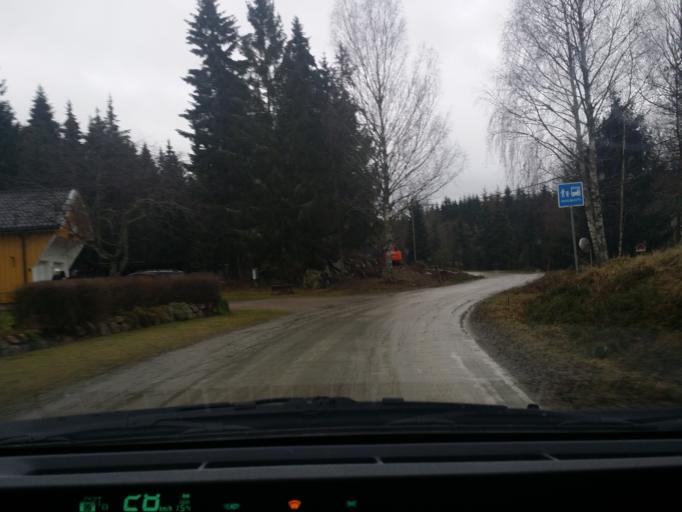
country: SE
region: Vaestmanland
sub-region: Vasteras
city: Skultuna
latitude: 59.7728
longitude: 16.3442
